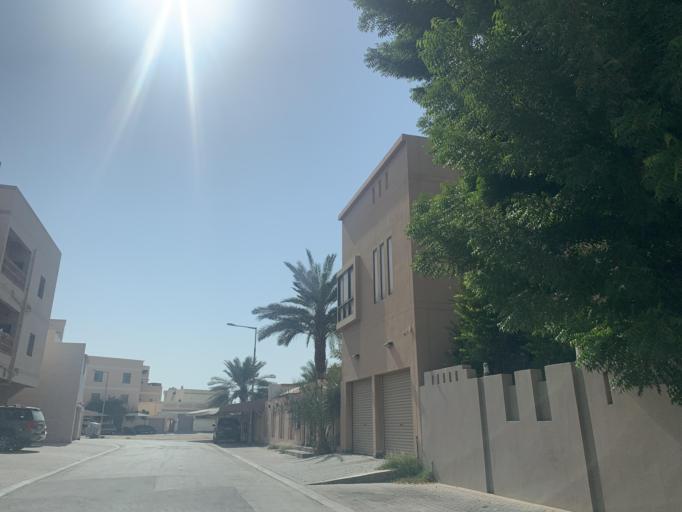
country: BH
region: Central Governorate
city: Madinat Hamad
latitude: 26.1367
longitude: 50.4952
